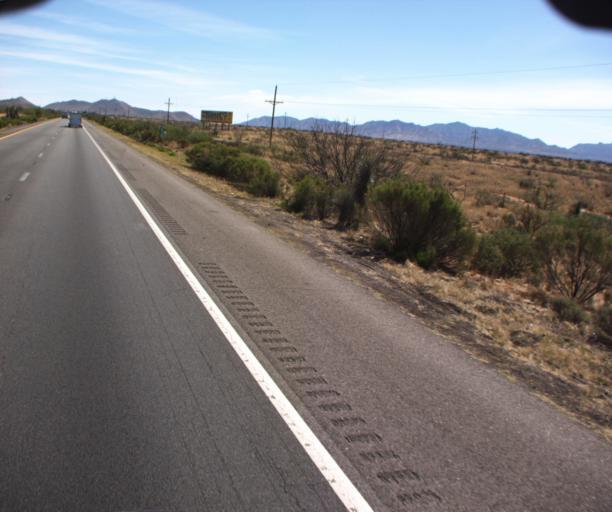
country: US
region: Arizona
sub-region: Cochise County
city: Saint David
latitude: 31.9878
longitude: -110.1890
